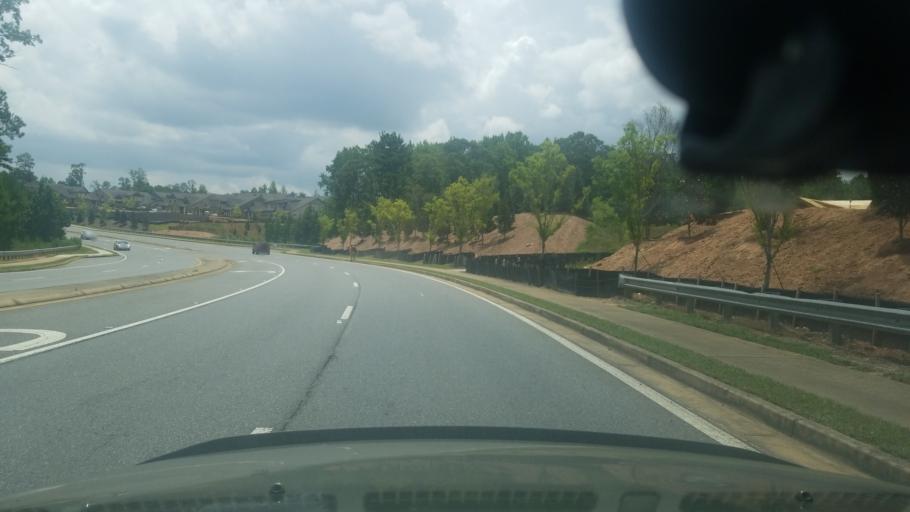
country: US
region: Georgia
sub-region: Fulton County
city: Johns Creek
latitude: 34.0969
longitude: -84.1695
